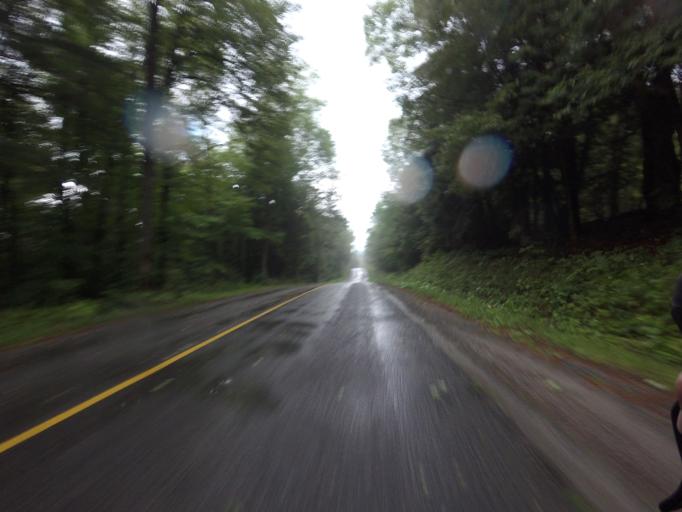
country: CA
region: Ontario
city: Perth
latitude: 45.0552
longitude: -76.5909
